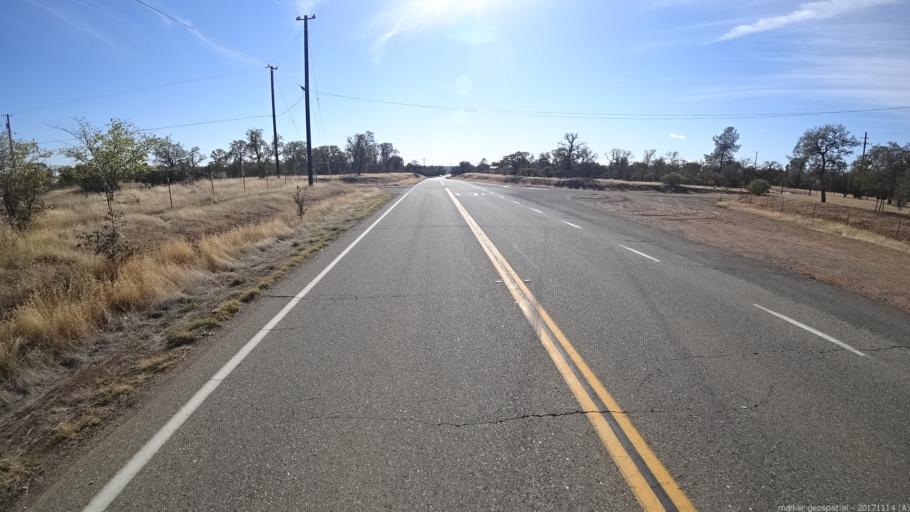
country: US
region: California
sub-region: Shasta County
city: Anderson
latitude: 40.4127
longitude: -122.4067
